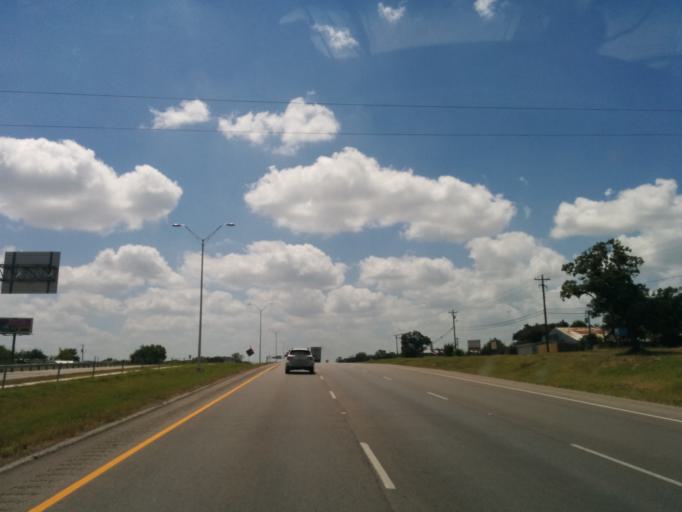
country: US
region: Texas
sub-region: Bastrop County
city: Bastrop
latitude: 30.1112
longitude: -97.3649
